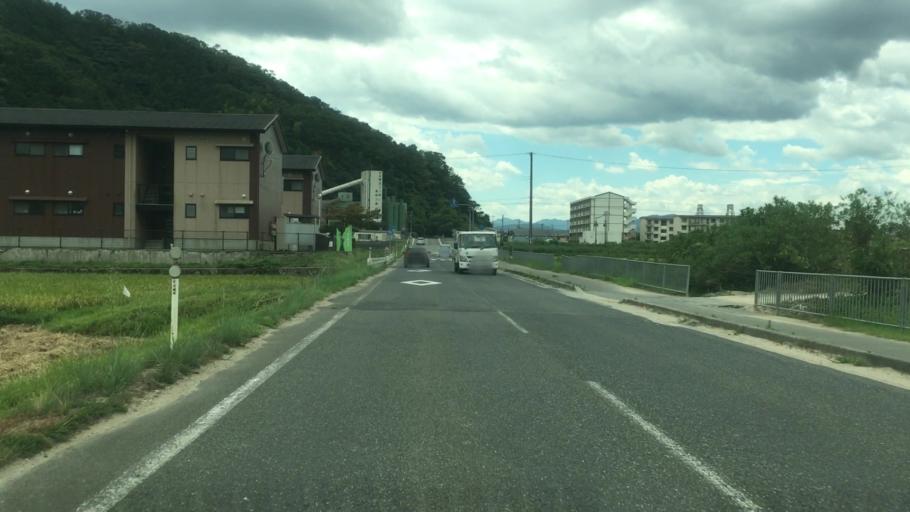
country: JP
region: Hyogo
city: Toyooka
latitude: 35.5506
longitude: 134.8424
